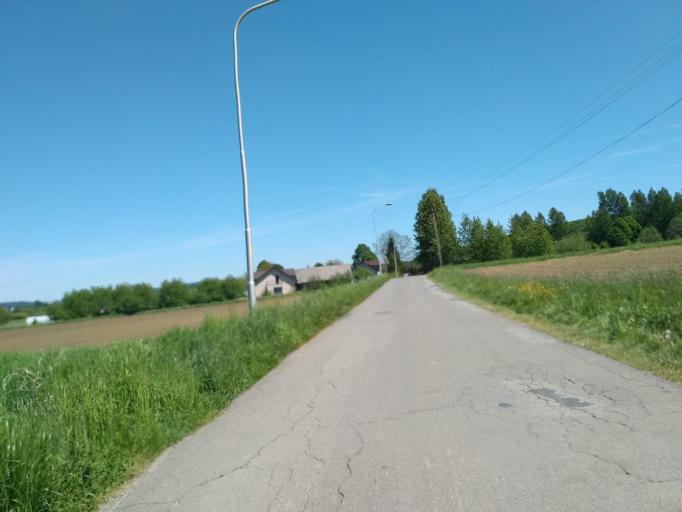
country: PL
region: Subcarpathian Voivodeship
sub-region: Powiat brzozowski
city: Turze Pole
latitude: 49.6452
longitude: 22.0087
